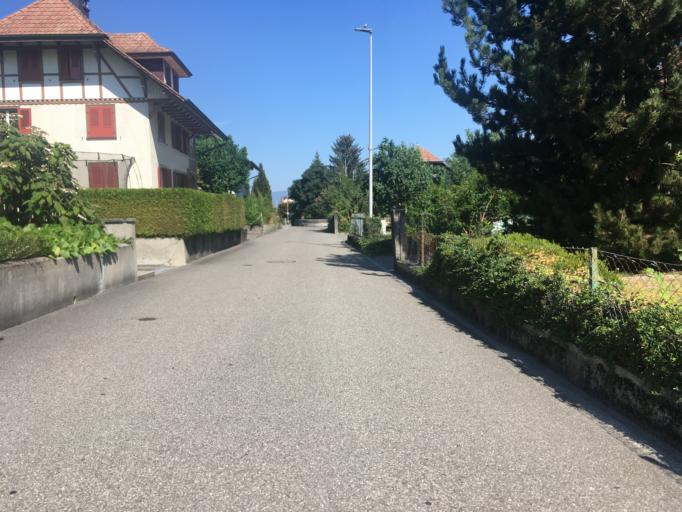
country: CH
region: Bern
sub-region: Emmental District
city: Kirchberg
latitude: 47.0868
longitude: 7.5804
